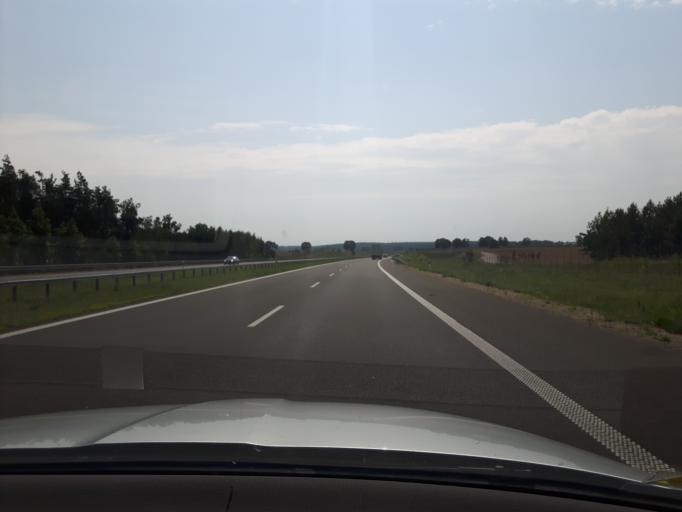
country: PL
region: Masovian Voivodeship
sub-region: Powiat mlawski
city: Wieczfnia Koscielna
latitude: 53.2389
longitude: 20.4231
